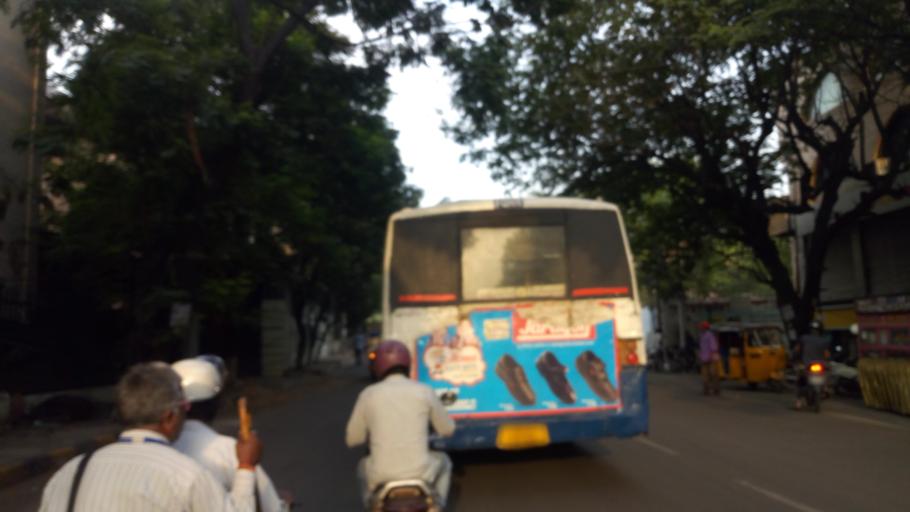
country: IN
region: Telangana
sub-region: Hyderabad
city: Hyderabad
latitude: 17.3985
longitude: 78.4725
